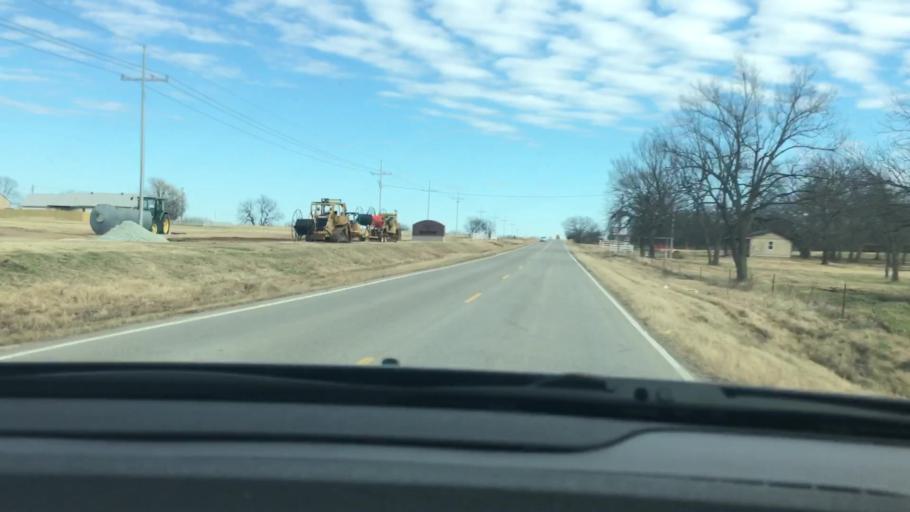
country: US
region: Oklahoma
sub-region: Garvin County
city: Stratford
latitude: 34.7966
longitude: -96.9312
